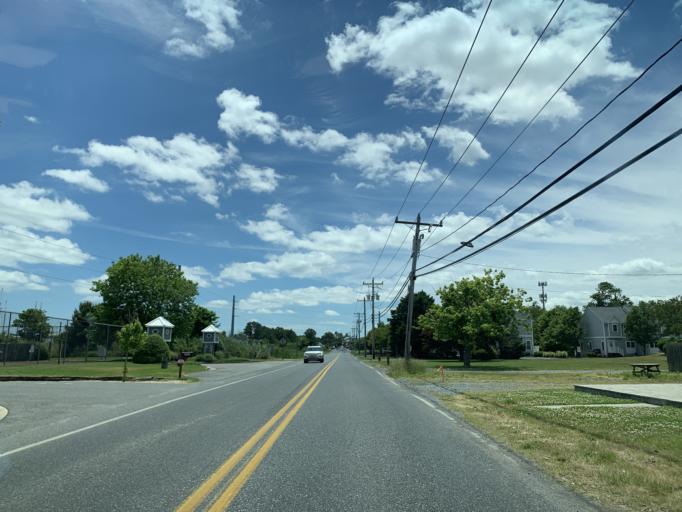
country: US
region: Maryland
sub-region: Worcester County
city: West Ocean City
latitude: 38.3306
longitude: -75.1069
